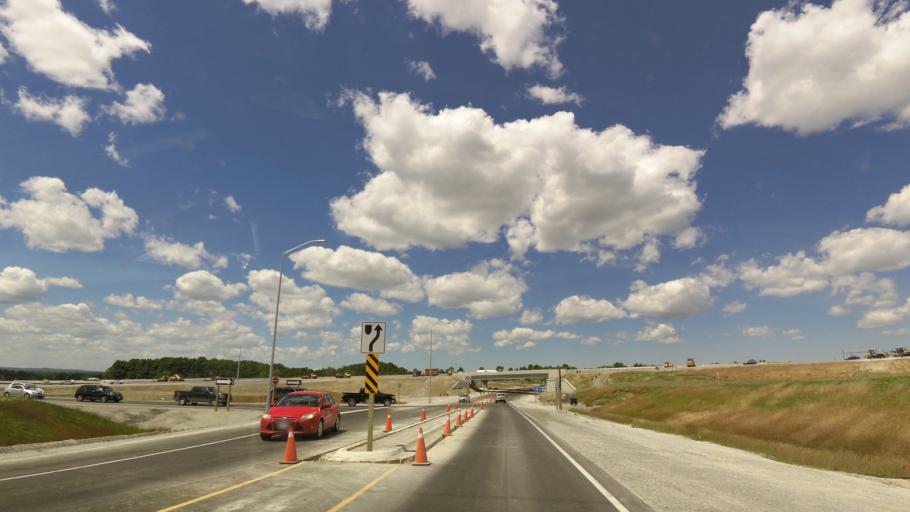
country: CA
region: Ontario
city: Oshawa
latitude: 43.9801
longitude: -78.8675
